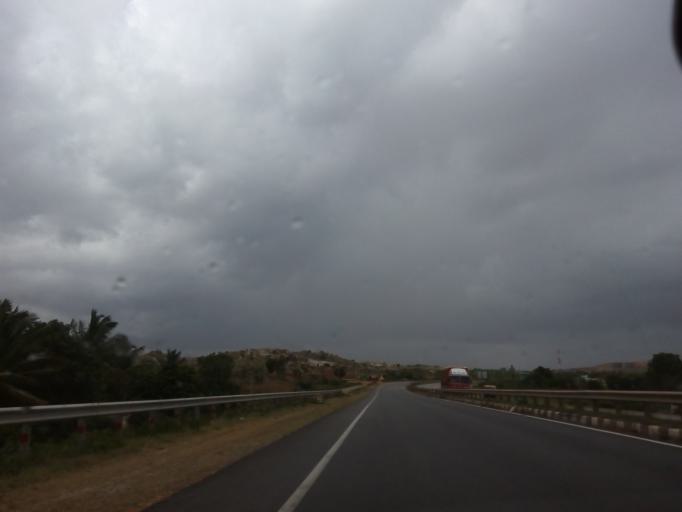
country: IN
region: Karnataka
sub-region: Chitradurga
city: Chitradurga
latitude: 14.2642
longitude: 76.3415
